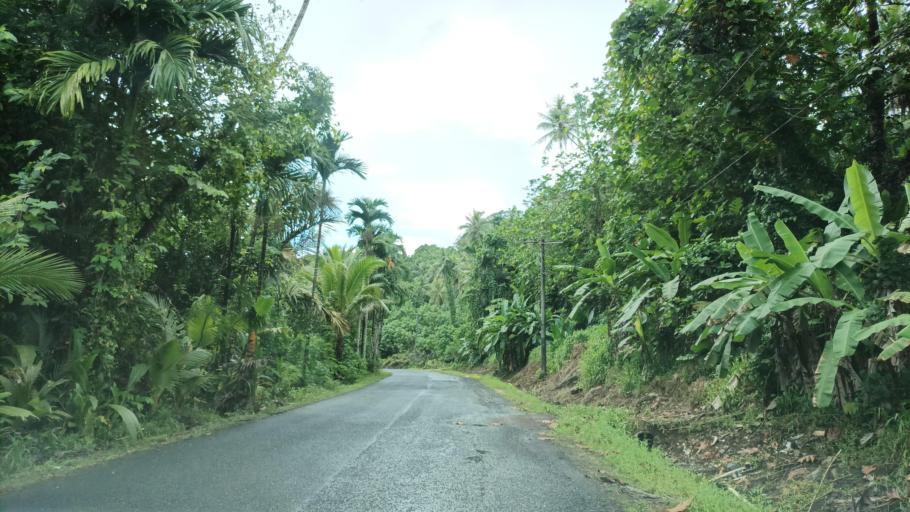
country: FM
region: Pohnpei
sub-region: Madolenihm Municipality
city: Madolenihm Municipality Government
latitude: 6.9140
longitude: 158.3213
